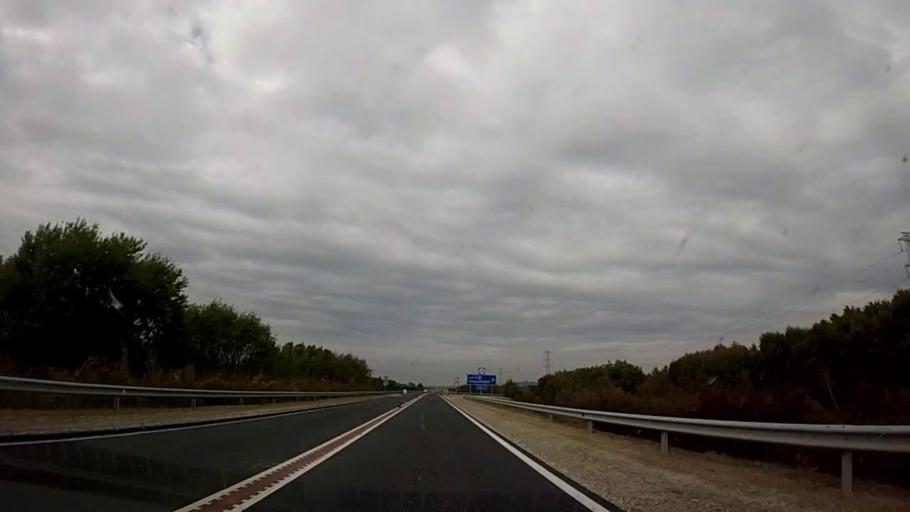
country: HR
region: Medimurska
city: Podturen
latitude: 46.5065
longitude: 16.5842
